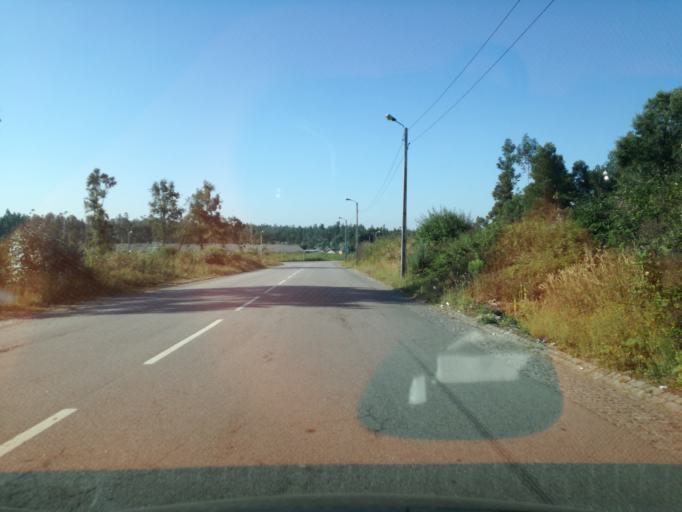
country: PT
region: Porto
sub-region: Maia
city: Nogueira
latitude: 41.2572
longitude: -8.5736
